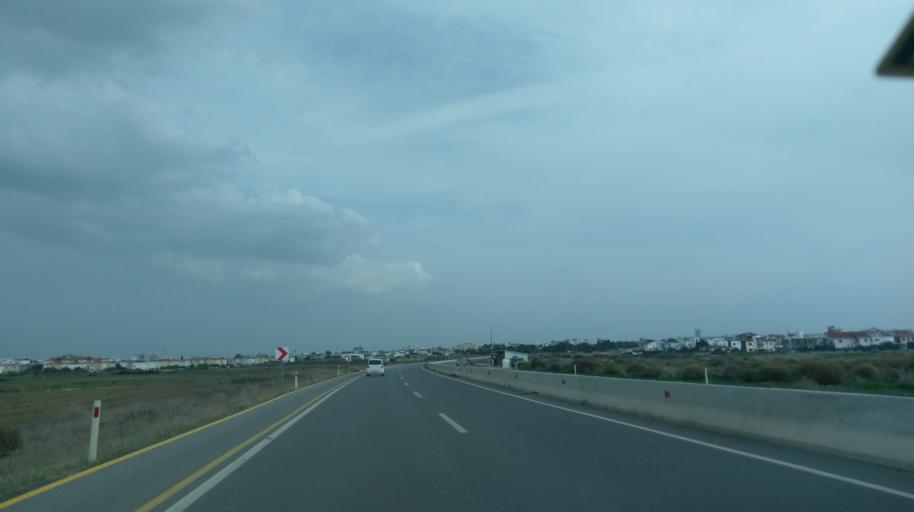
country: CY
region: Lefkosia
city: Nicosia
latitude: 35.1984
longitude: 33.3098
